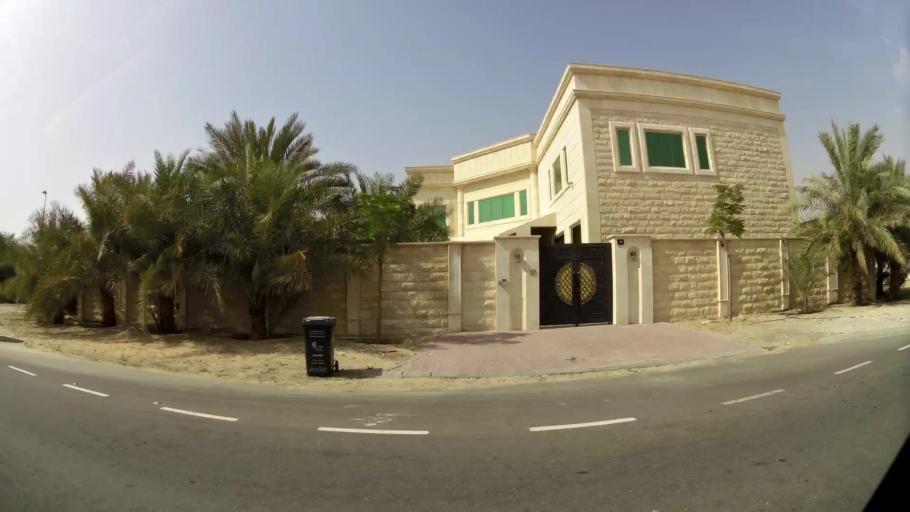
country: AE
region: Ash Shariqah
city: Sharjah
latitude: 25.2471
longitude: 55.4365
